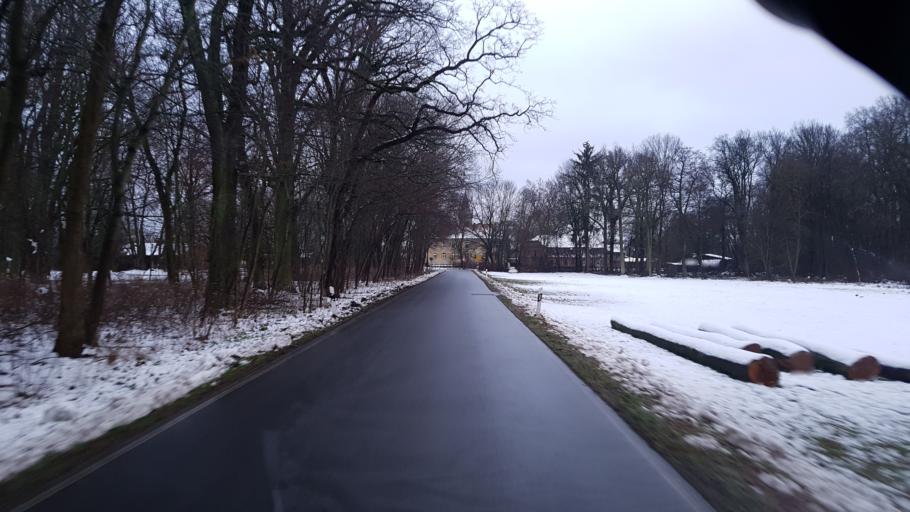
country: DE
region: Brandenburg
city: Luckau
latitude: 51.7970
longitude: 13.7347
